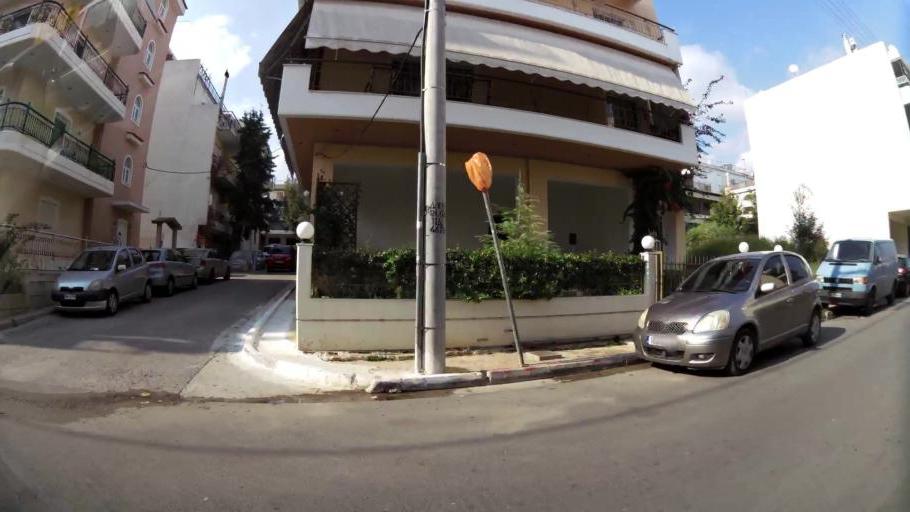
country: GR
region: Attica
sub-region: Nomarchia Athinas
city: Petroupolis
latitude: 38.0485
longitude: 23.6952
